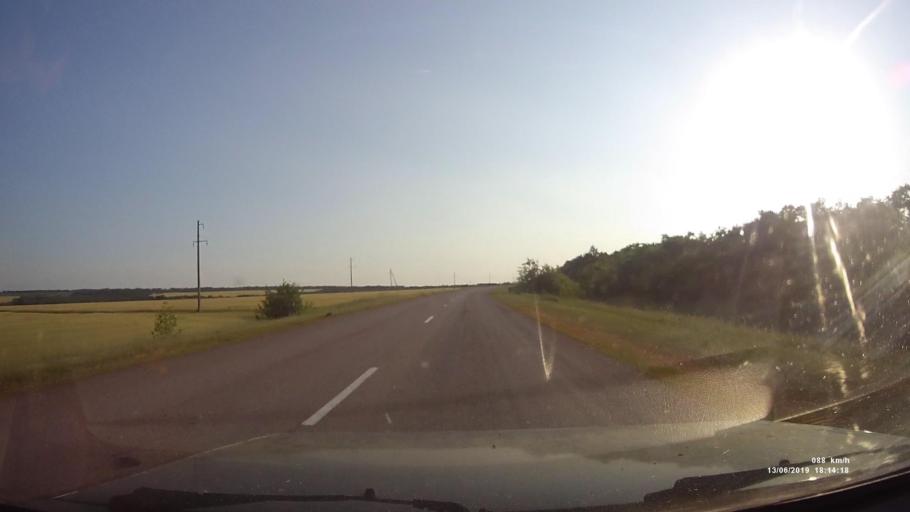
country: RU
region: Rostov
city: Kazanskaya
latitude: 49.9342
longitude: 41.3790
